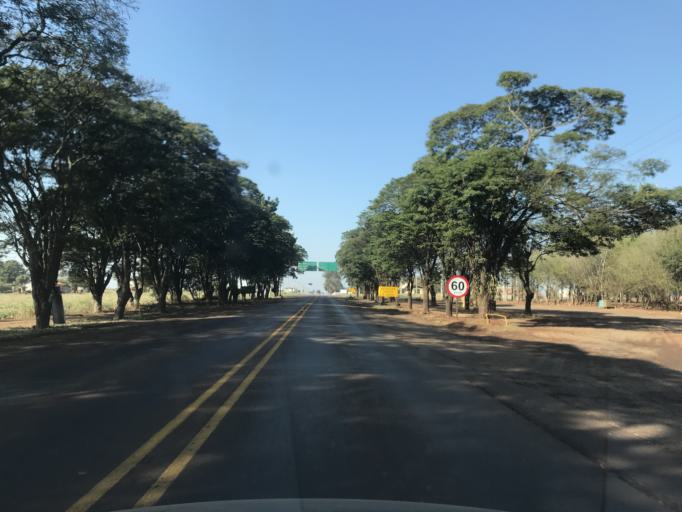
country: BR
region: Parana
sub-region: Palotina
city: Palotina
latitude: -24.3054
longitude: -53.8332
